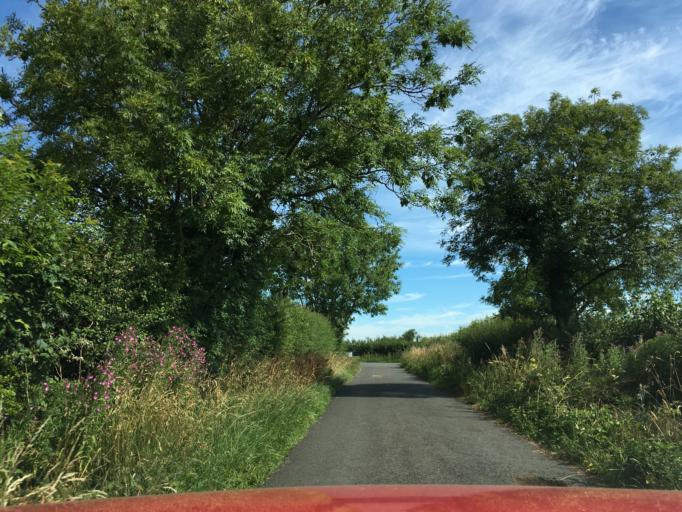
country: GB
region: England
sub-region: South Gloucestershire
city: Horton
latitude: 51.5421
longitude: -2.3654
